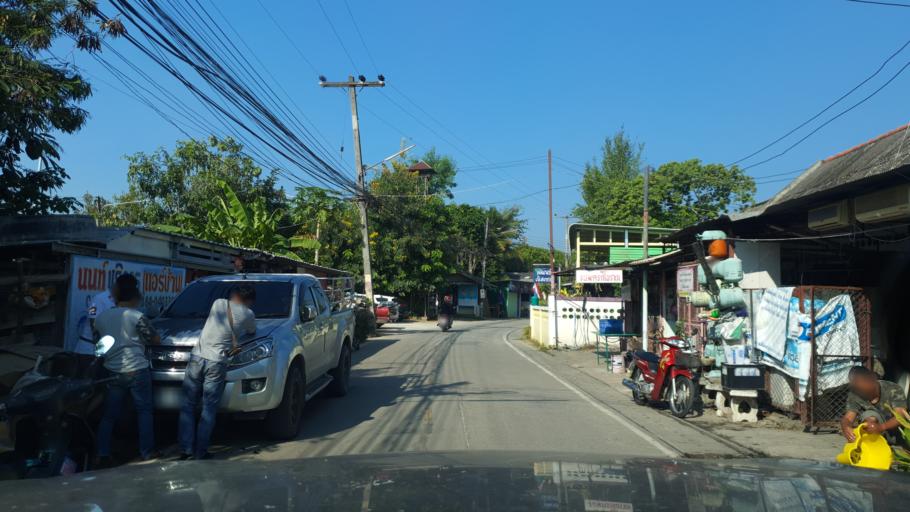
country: TH
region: Chiang Mai
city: Hang Dong
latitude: 18.7102
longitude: 98.9463
